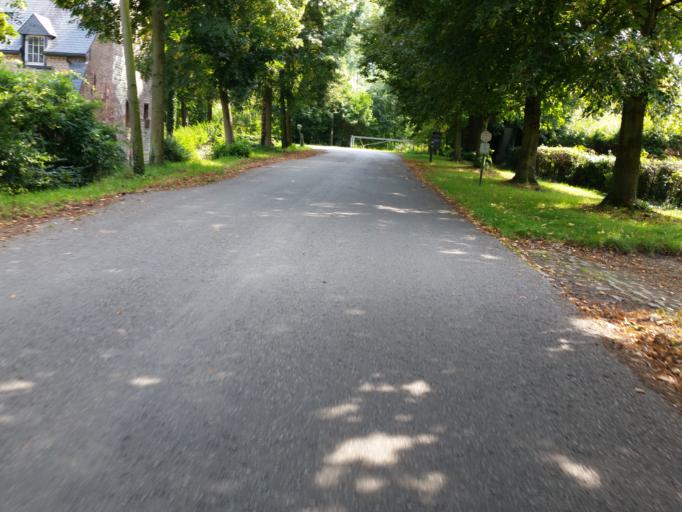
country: BE
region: Flanders
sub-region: Provincie Vlaams-Brabant
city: Zemst
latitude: 50.9600
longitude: 4.4784
